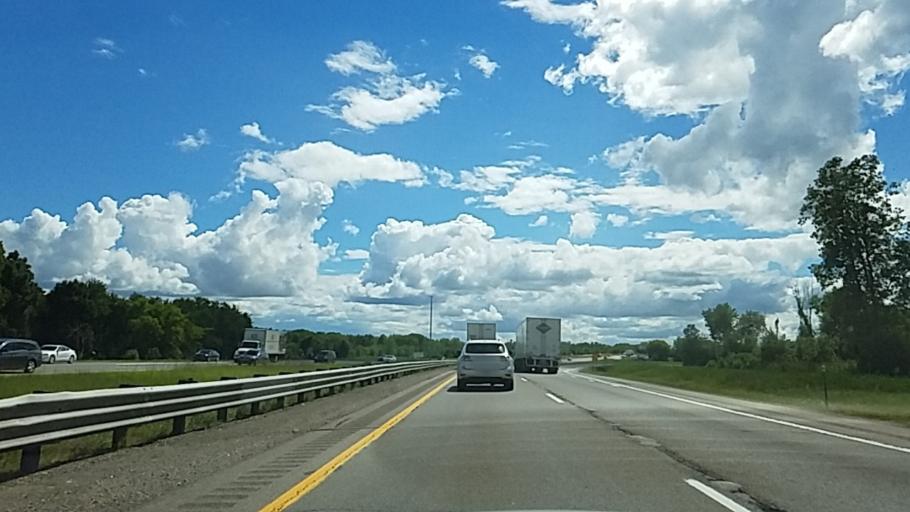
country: US
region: Michigan
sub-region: Livingston County
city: Whitmore Lake
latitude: 42.4474
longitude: -83.7527
